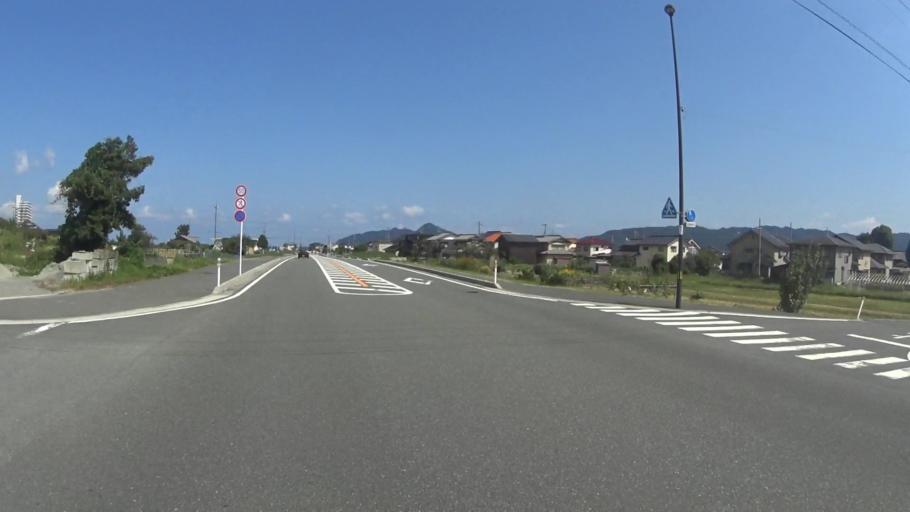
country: JP
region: Kyoto
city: Miyazu
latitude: 35.5831
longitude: 135.2011
